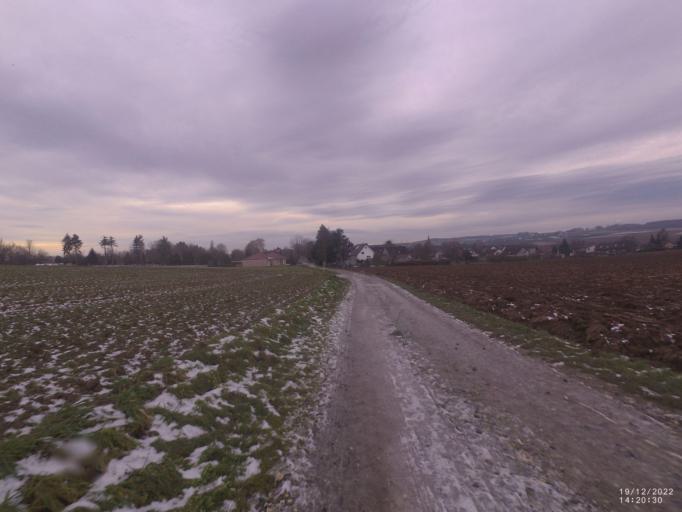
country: DE
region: Rheinland-Pfalz
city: Unkel
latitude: 50.6078
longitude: 7.1654
